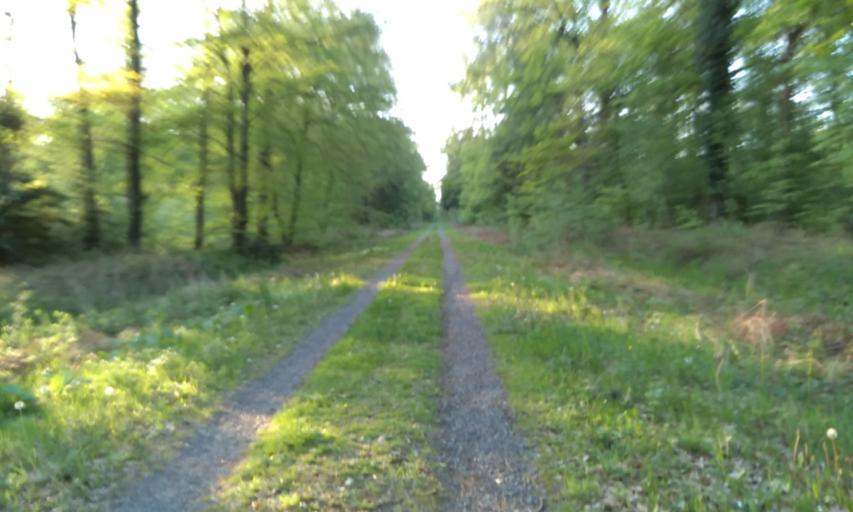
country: DE
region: Lower Saxony
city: Harsefeld
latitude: 53.4151
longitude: 9.5040
